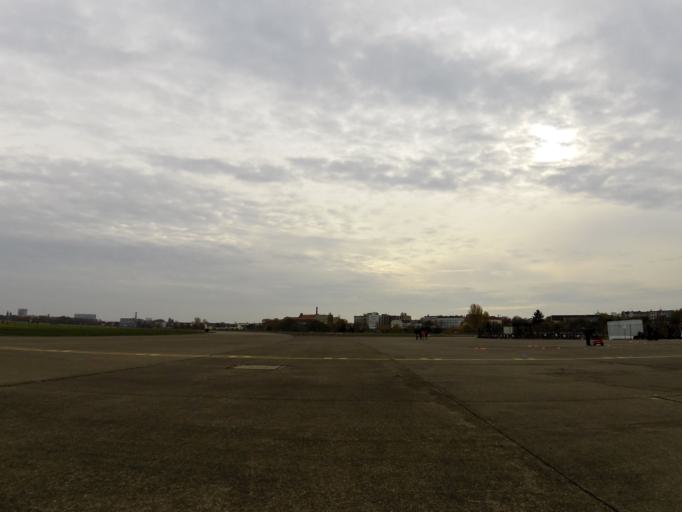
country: DE
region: Berlin
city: Tempelhof Bezirk
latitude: 52.4729
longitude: 13.3898
